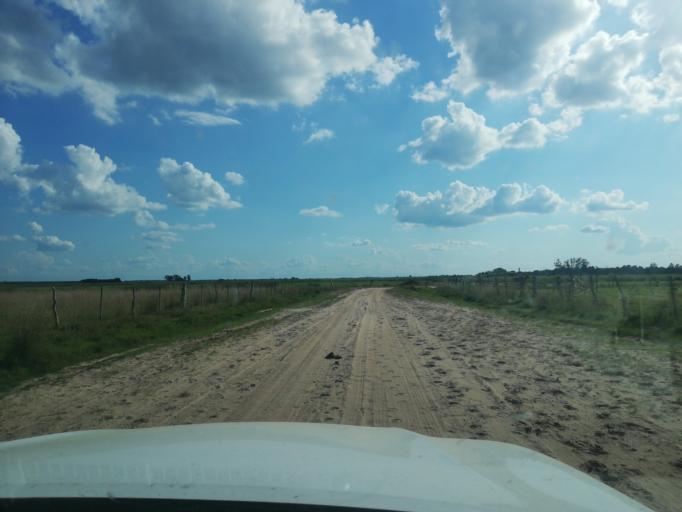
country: AR
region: Corrientes
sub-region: Departamento de San Miguel
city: San Miguel
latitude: -27.9939
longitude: -57.5725
